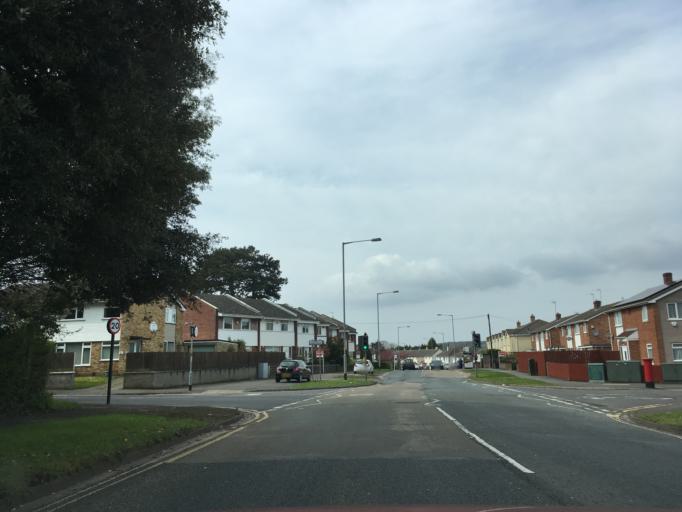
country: GB
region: England
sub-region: Bristol
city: Bristol
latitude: 51.5097
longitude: -2.6130
